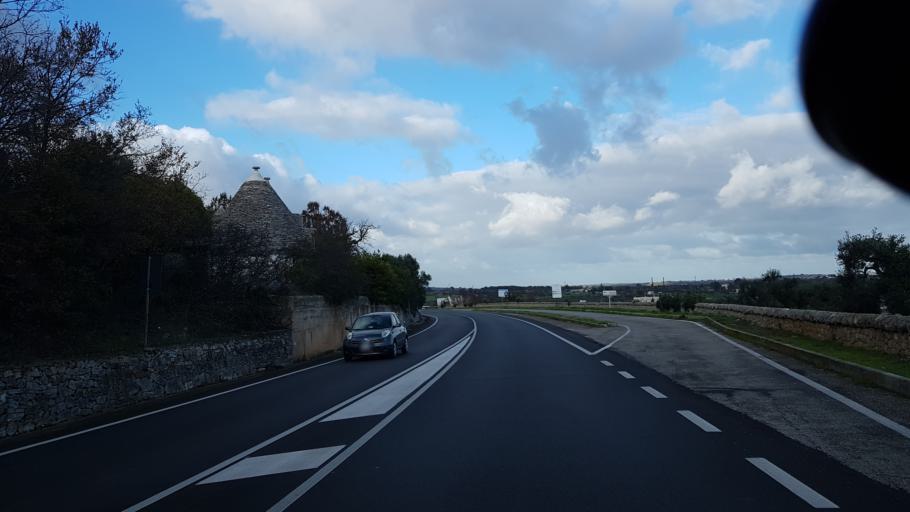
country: IT
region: Apulia
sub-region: Provincia di Bari
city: Alberobello
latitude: 40.7922
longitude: 17.2430
